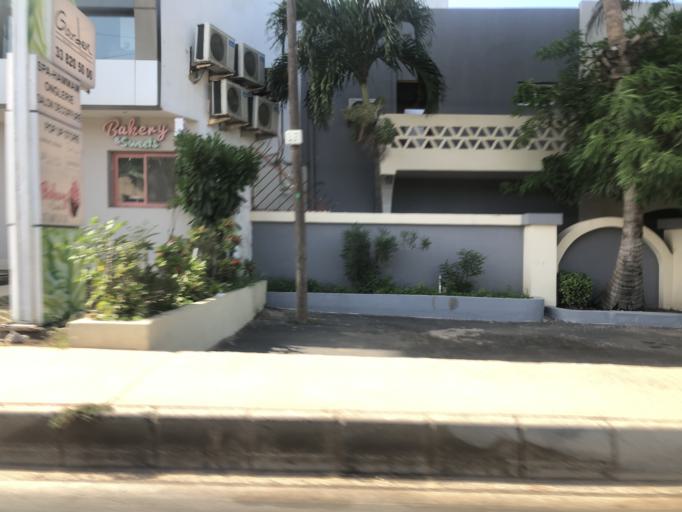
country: SN
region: Dakar
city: Mermoz Boabab
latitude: 14.7506
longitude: -17.5034
